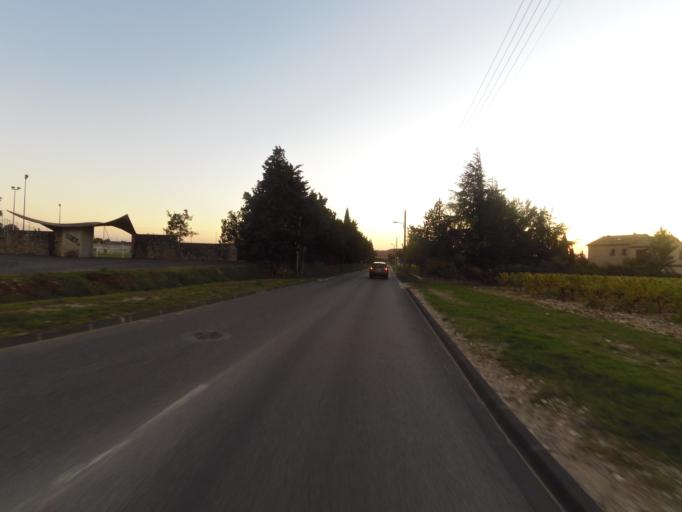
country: FR
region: Provence-Alpes-Cote d'Azur
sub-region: Departement du Vaucluse
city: Bedoin
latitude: 44.1183
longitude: 5.1792
